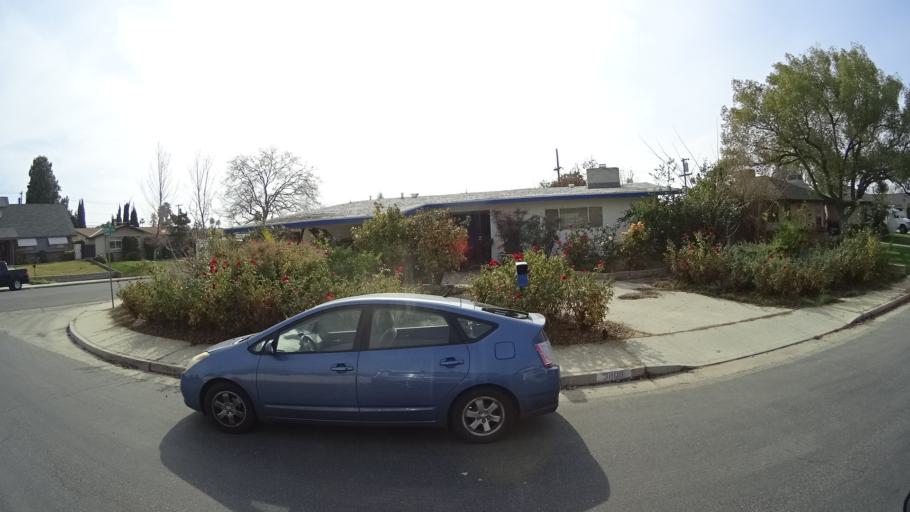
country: US
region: California
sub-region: Kern County
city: Oildale
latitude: 35.4075
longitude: -118.9504
